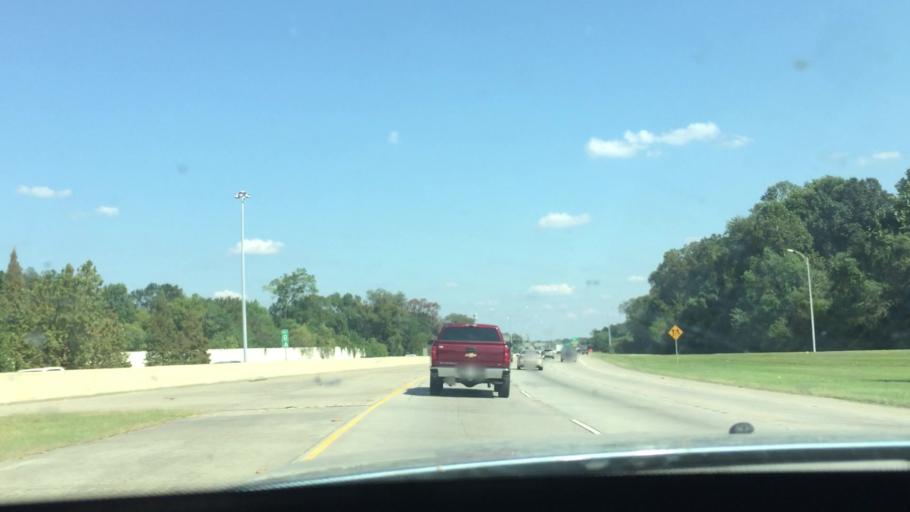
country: US
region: Louisiana
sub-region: East Baton Rouge Parish
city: Westminster
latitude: 30.4185
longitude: -91.1117
